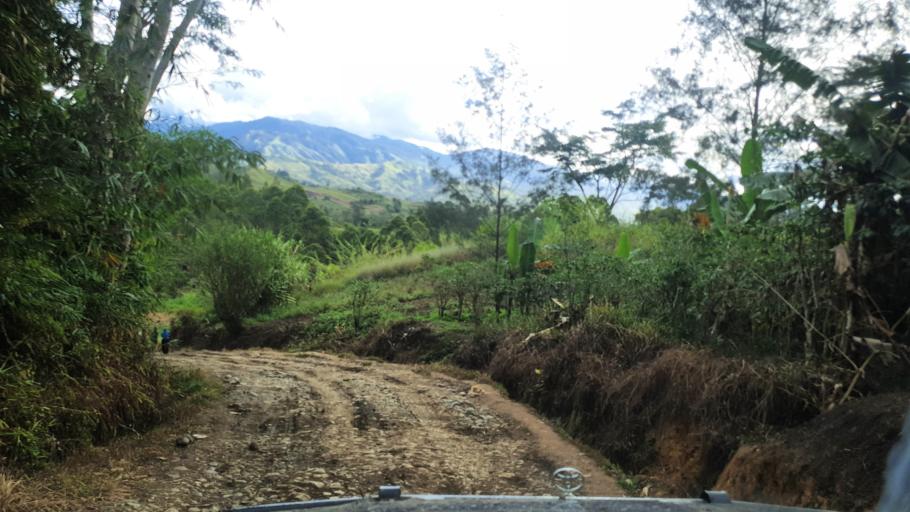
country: PG
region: Jiwaka
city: Minj
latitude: -5.9371
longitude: 144.8075
